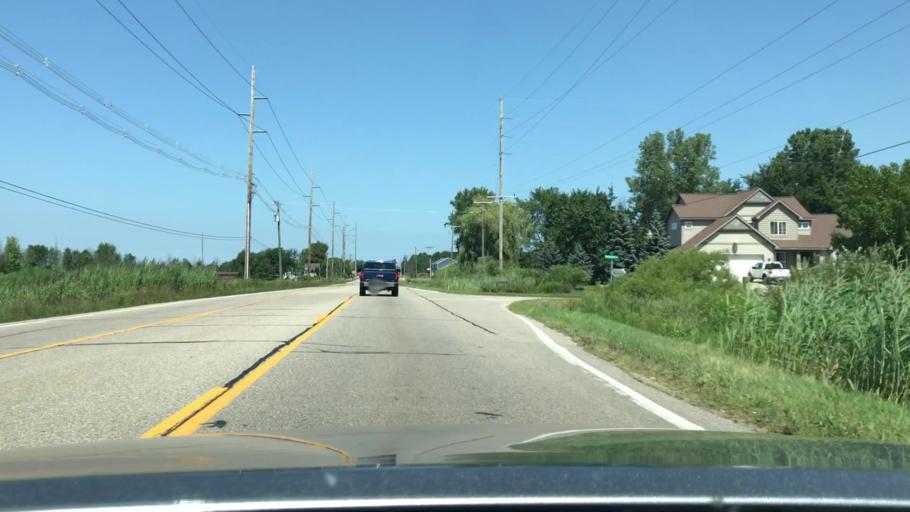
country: US
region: Michigan
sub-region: Ottawa County
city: Holland
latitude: 42.8368
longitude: -86.0788
